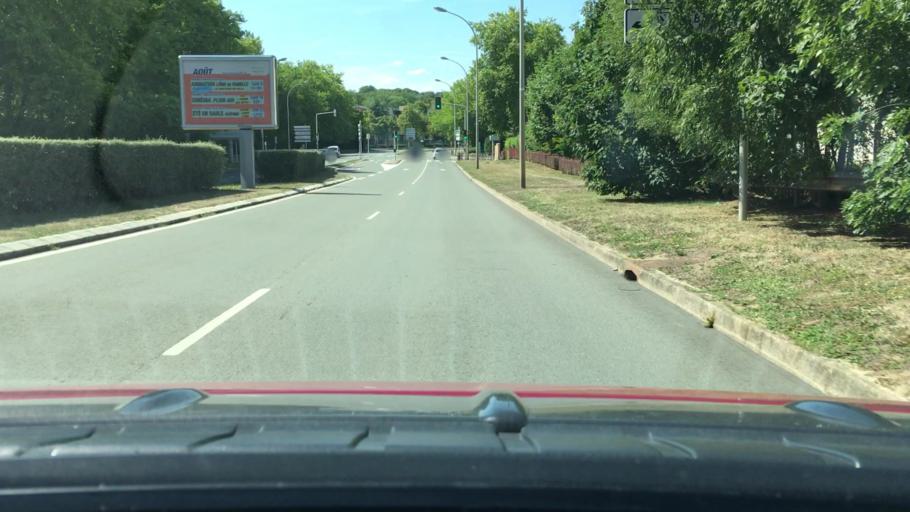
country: FR
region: Ile-de-France
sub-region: Departement des Yvelines
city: Bois-d'Arcy
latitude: 48.7929
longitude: 2.0380
